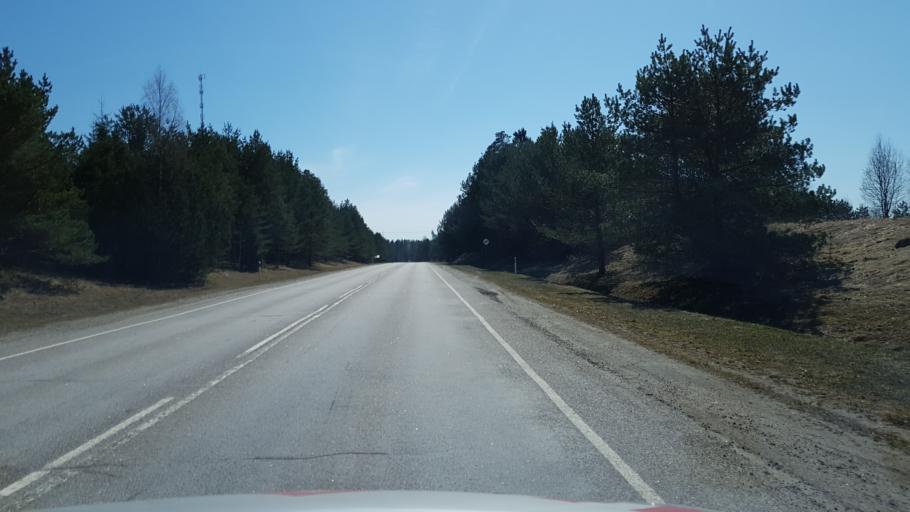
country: EE
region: Ida-Virumaa
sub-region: Johvi vald
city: Johvi
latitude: 59.1672
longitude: 27.3520
